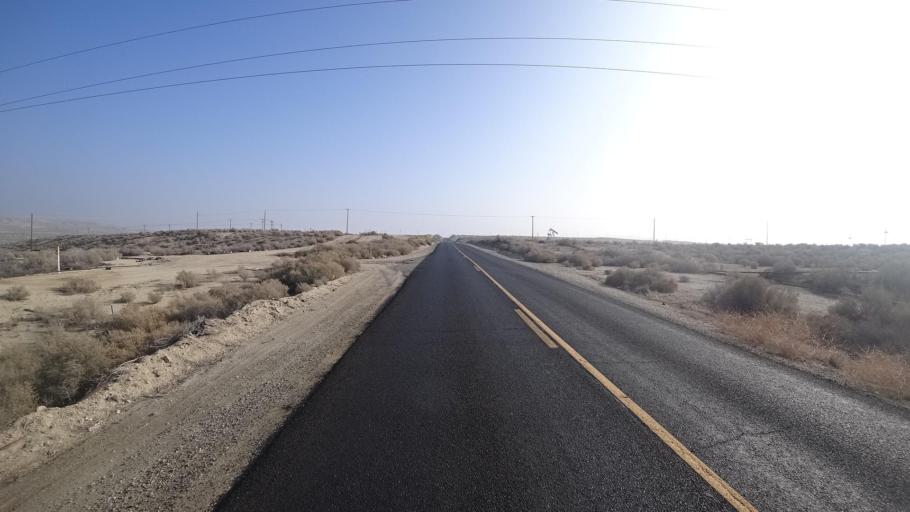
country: US
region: California
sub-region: Kern County
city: Ford City
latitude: 35.1806
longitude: -119.4742
